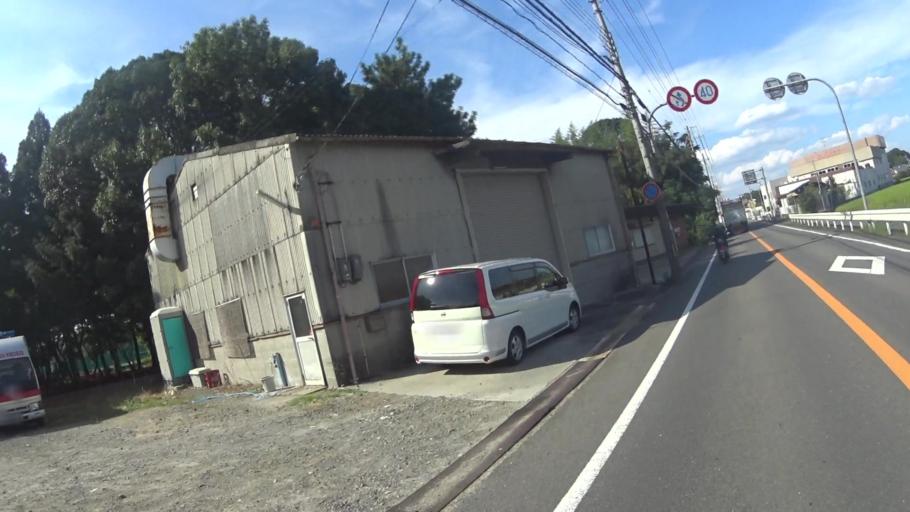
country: JP
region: Kyoto
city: Tanabe
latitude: 34.8607
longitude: 135.7453
